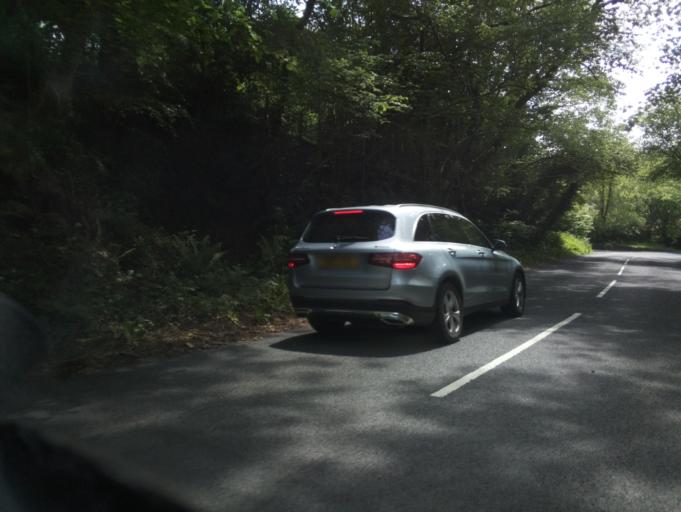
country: GB
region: England
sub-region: Herefordshire
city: Llanrothal
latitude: 51.8858
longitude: -2.7743
